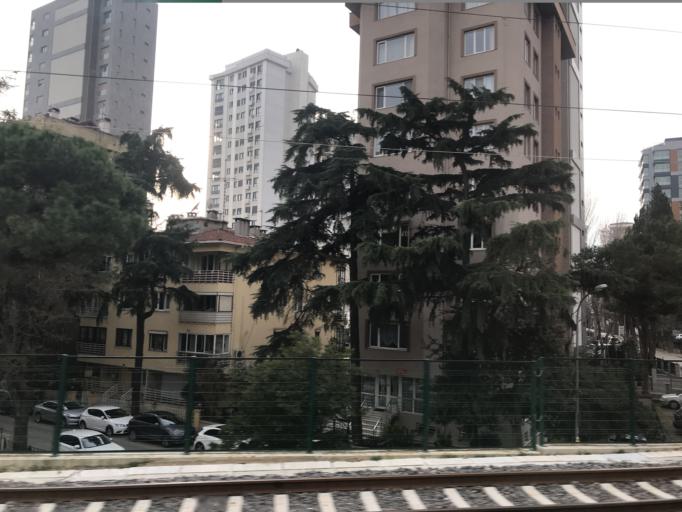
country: TR
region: Istanbul
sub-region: Atasehir
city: Atasehir
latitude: 40.9573
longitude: 29.0903
